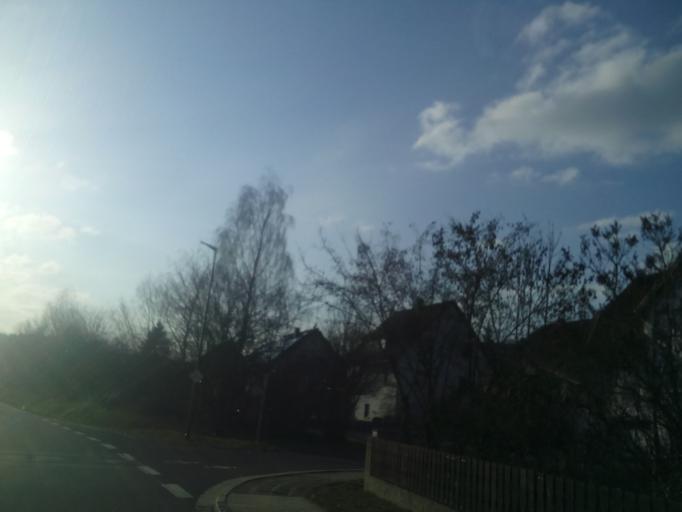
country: DE
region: Bavaria
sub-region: Regierungsbezirk Mittelfranken
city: Gutenstetten
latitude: 49.6183
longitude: 10.6282
